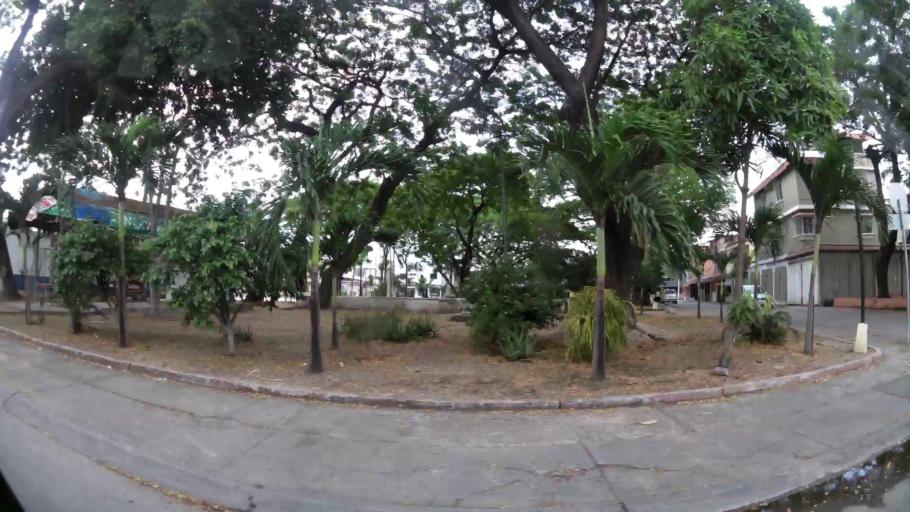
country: EC
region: Guayas
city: Eloy Alfaro
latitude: -2.1194
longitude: -79.8922
